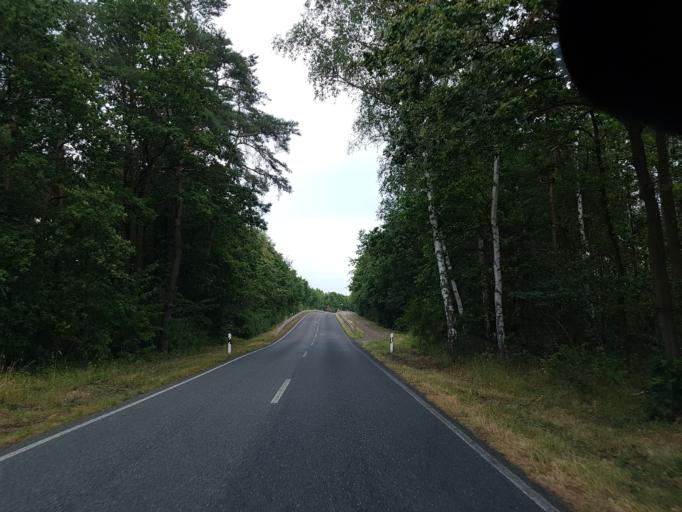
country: DE
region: Brandenburg
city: Schipkau
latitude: 51.5555
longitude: 13.9114
